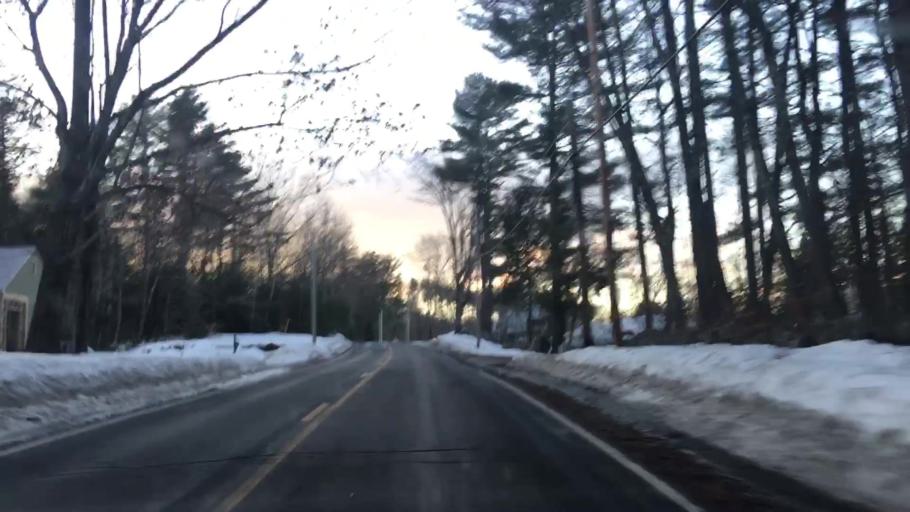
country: US
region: Maine
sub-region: York County
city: Newfield
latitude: 43.6422
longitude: -70.9109
